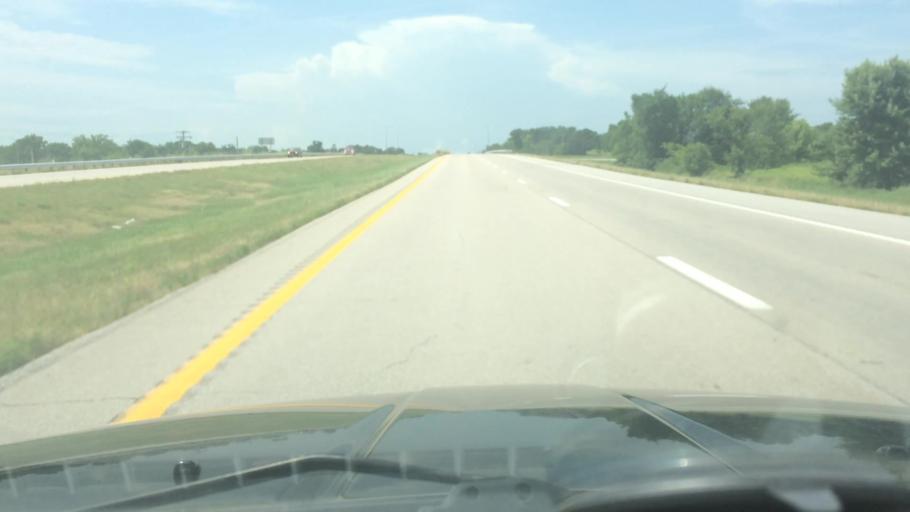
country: US
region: Missouri
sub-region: Polk County
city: Humansville
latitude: 37.7921
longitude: -93.5865
